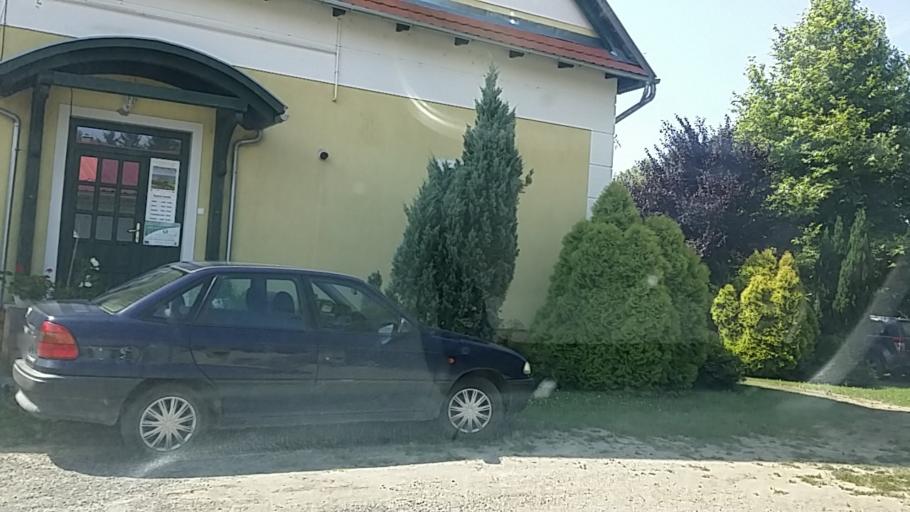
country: HR
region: Medimurska
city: Podturen
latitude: 46.5012
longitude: 16.5770
